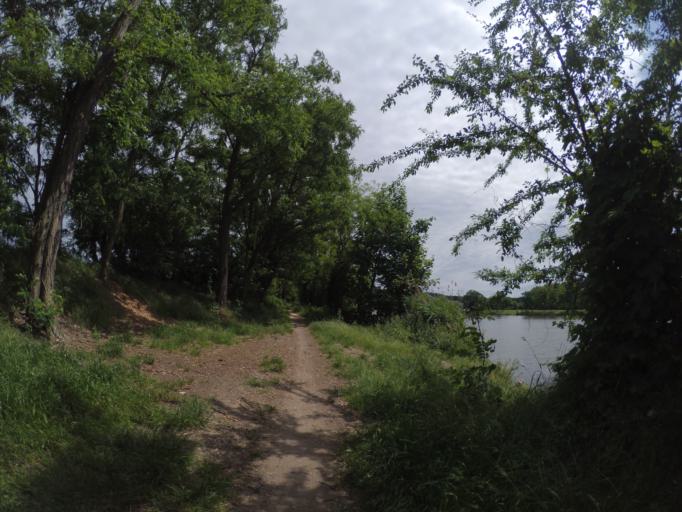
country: CZ
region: Central Bohemia
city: Lysa nad Labem
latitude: 50.1793
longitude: 14.8532
